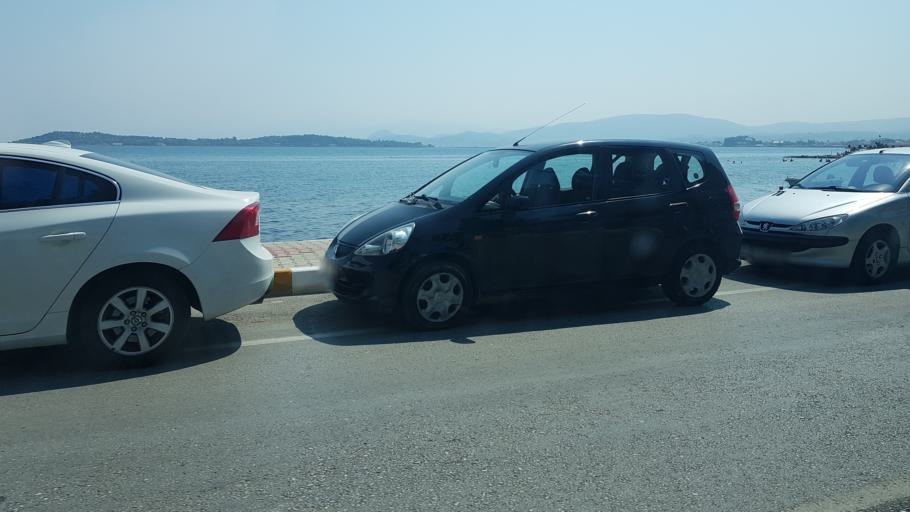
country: TR
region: Izmir
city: Urla
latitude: 38.3745
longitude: 26.7615
